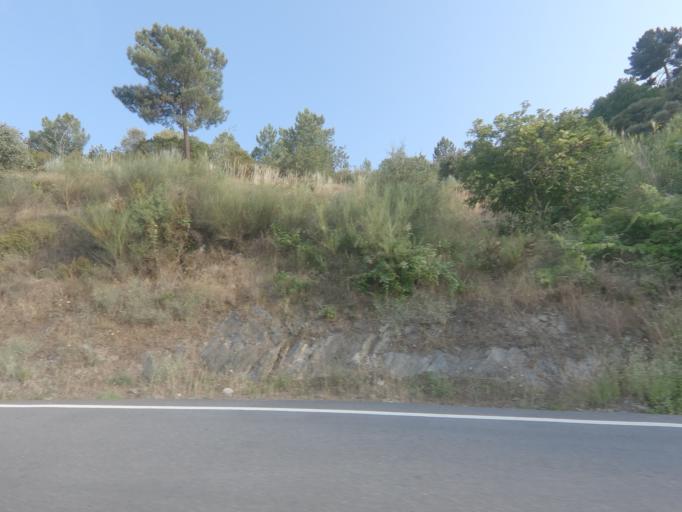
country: PT
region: Viseu
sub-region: Tabuaco
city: Tabuaco
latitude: 41.1500
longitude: -7.6236
